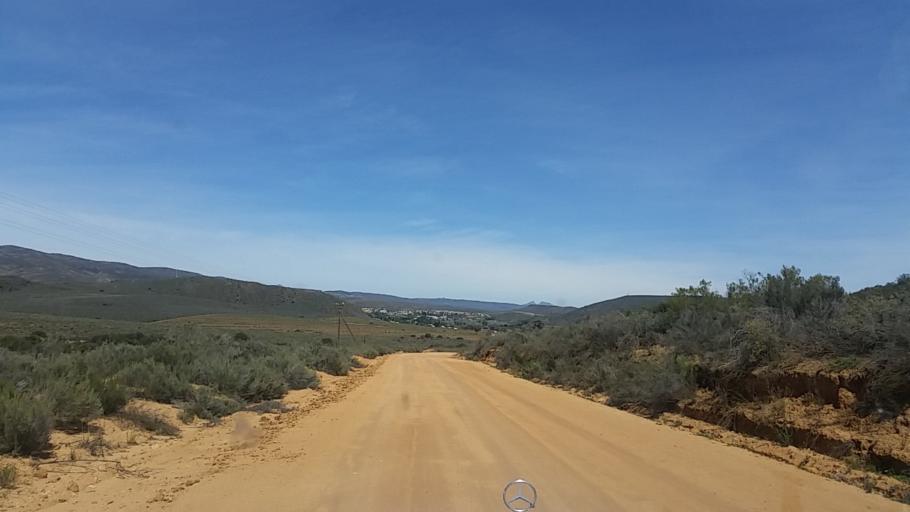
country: ZA
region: Western Cape
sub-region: Eden District Municipality
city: Knysna
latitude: -33.6377
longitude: 23.1513
